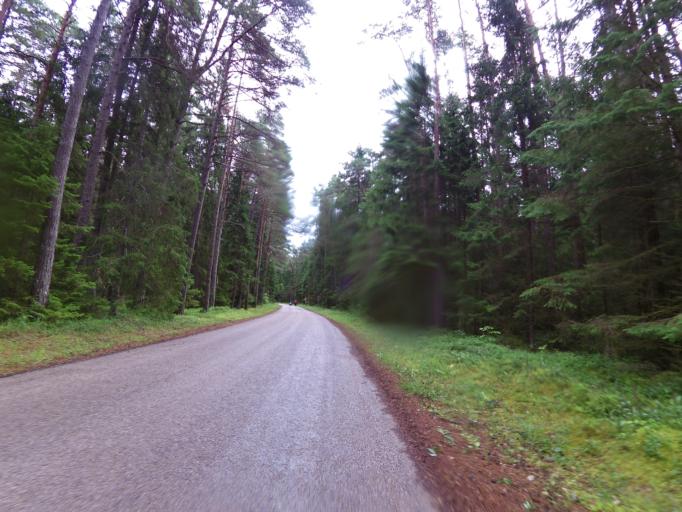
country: EE
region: Laeaene
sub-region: Vormsi vald
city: Hullo
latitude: 58.9996
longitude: 23.2432
